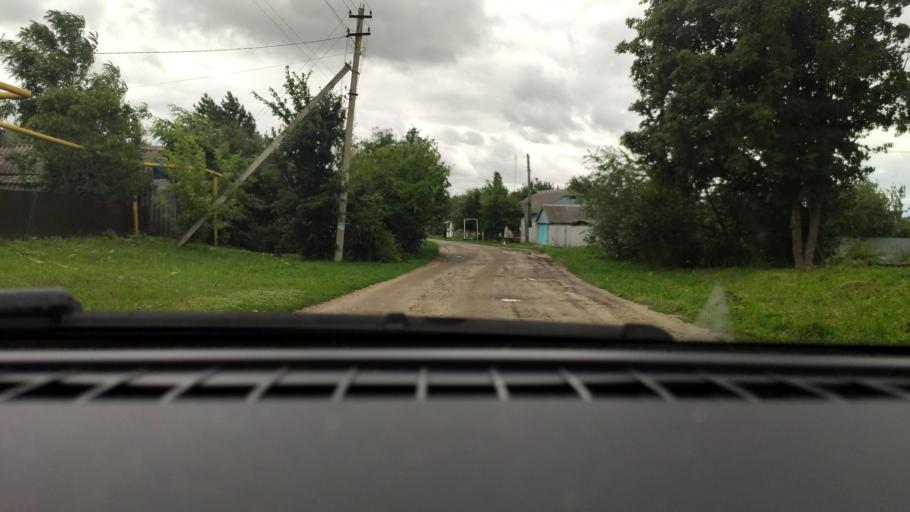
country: RU
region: Voronezj
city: Zemlyansk
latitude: 51.9097
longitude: 38.7254
